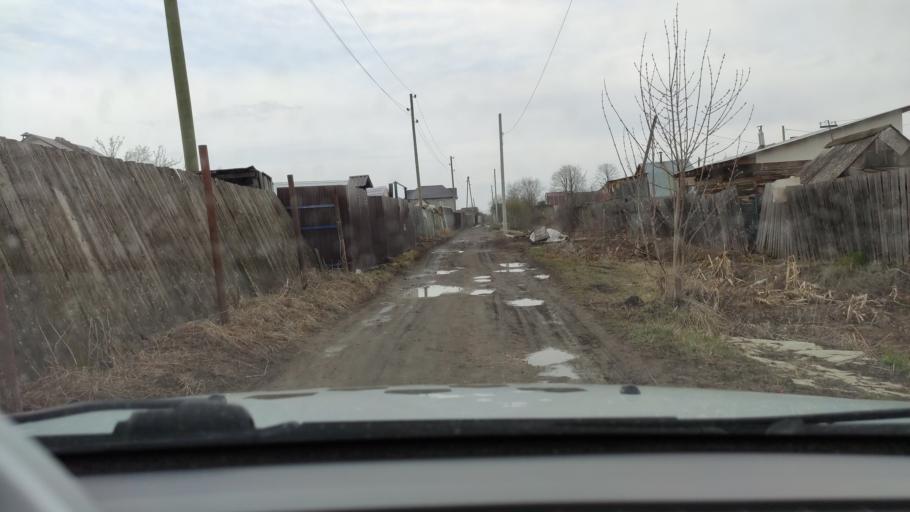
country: RU
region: Perm
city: Kondratovo
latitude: 57.9843
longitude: 56.1012
